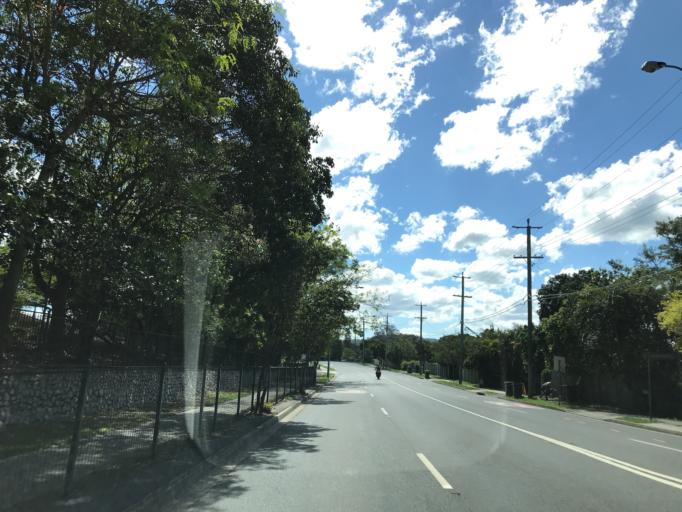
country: AU
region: Queensland
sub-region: Moreton Bay
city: Ferny Hills
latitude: -27.4450
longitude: 152.9494
